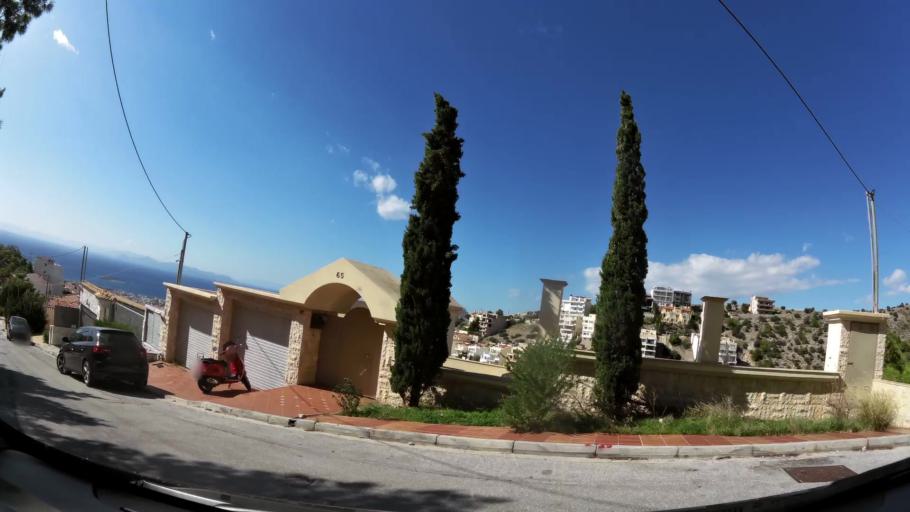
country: GR
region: Attica
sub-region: Nomarchia Anatolikis Attikis
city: Voula
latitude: 37.8595
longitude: 23.7823
